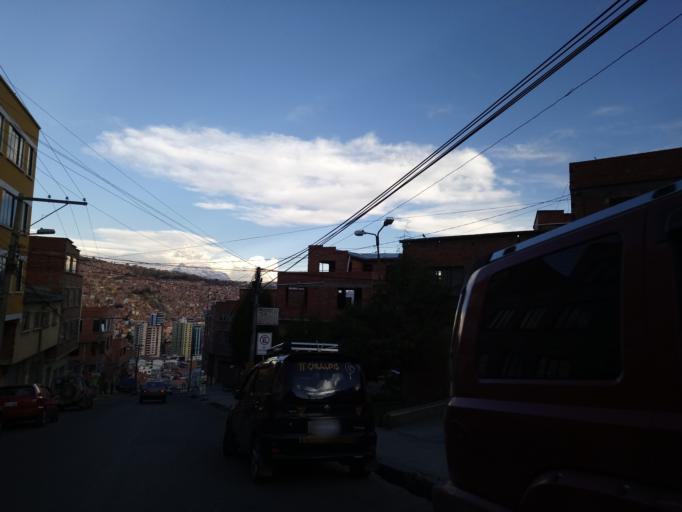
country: BO
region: La Paz
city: La Paz
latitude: -16.4873
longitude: -68.1270
